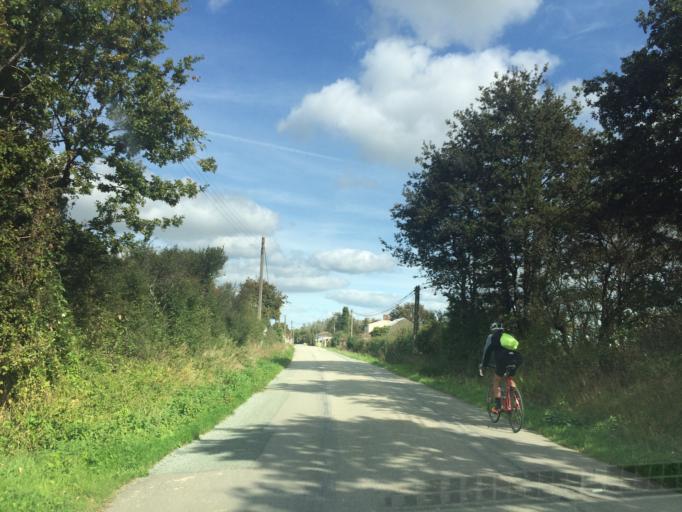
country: FR
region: Pays de la Loire
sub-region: Departement de la Loire-Atlantique
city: Chemere
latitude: 47.0993
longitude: -1.9131
